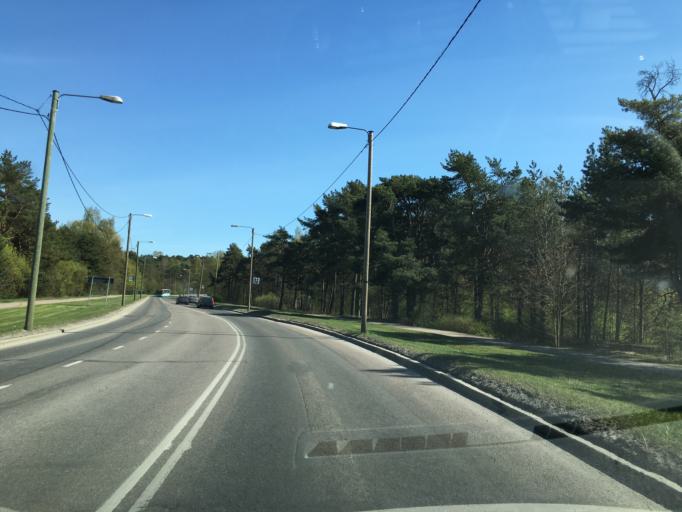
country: EE
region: Harju
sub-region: Saue vald
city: Laagri
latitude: 59.3926
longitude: 24.6748
